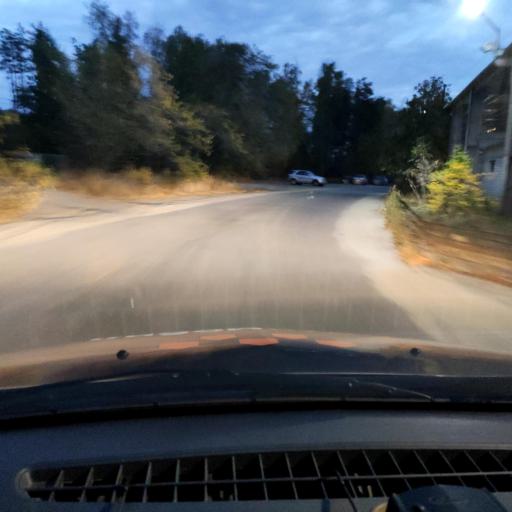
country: RU
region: Voronezj
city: Pridonskoy
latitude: 51.6744
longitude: 39.1023
